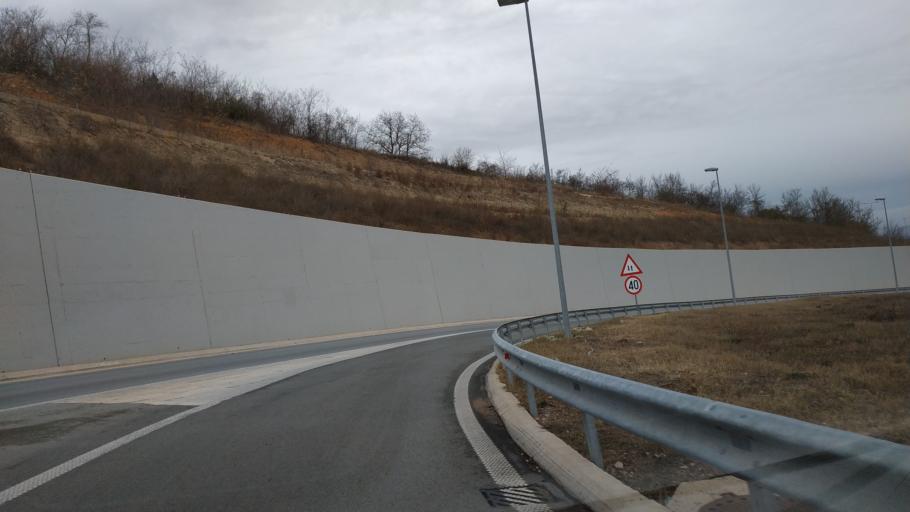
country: RS
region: Central Serbia
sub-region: Pirotski Okrug
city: Bela Palanka
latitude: 43.2355
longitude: 22.3148
